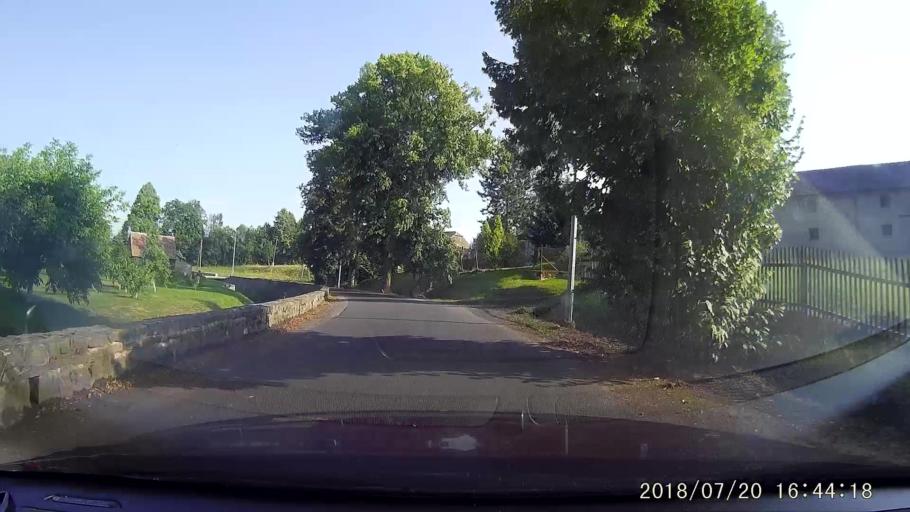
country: PL
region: Lower Silesian Voivodeship
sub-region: Powiat lubanski
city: Siekierczyn
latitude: 51.0690
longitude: 15.1649
